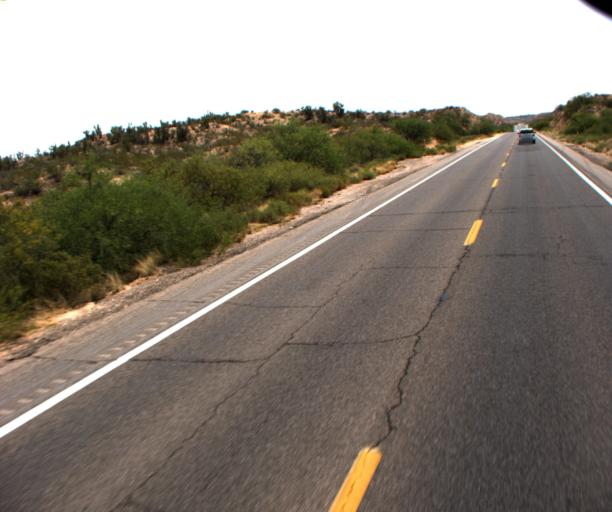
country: US
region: Arizona
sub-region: Gila County
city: Globe
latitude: 33.3478
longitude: -110.6282
